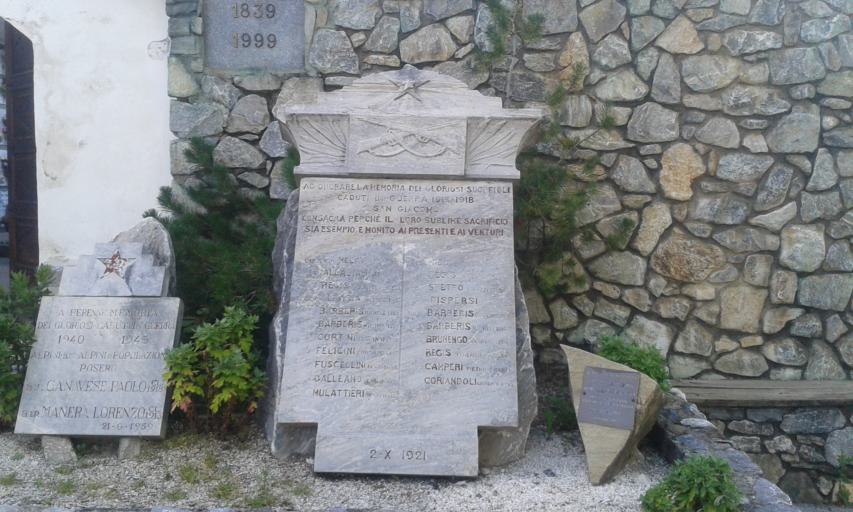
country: IT
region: Piedmont
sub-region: Provincia di Cuneo
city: Roburent
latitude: 44.2946
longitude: 7.8757
